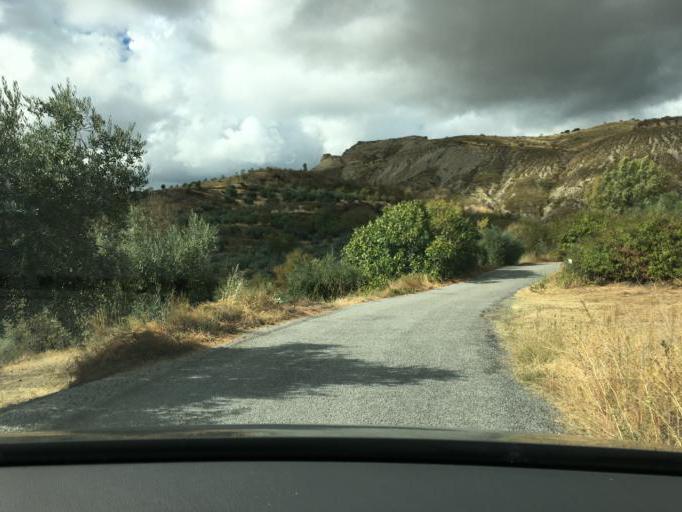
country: ES
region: Andalusia
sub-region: Provincia de Granada
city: Beas de Granada
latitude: 37.2109
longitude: -3.4655
